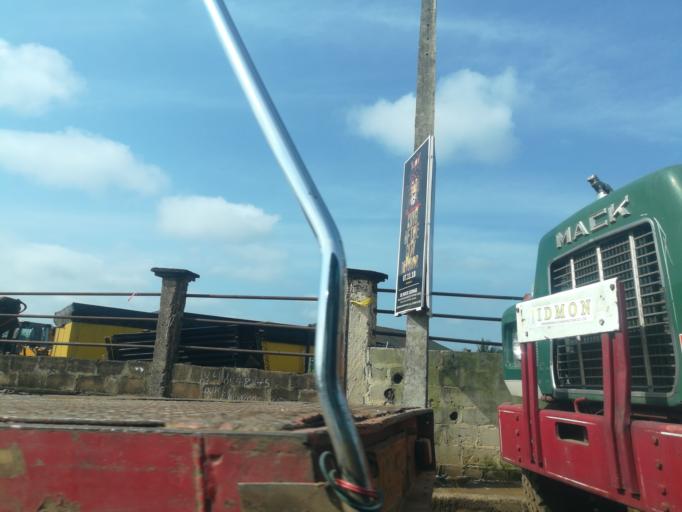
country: NG
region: Oyo
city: Ibadan
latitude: 7.3372
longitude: 3.8548
